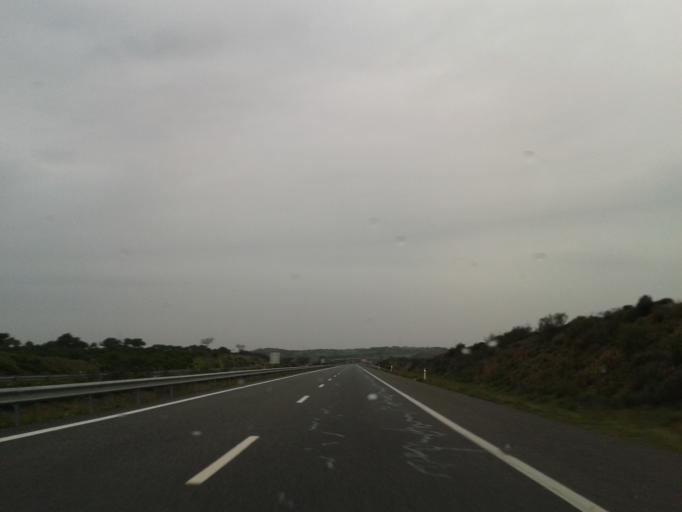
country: PT
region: Beja
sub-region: Ourique
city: Ourique
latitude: 37.5415
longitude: -8.1861
